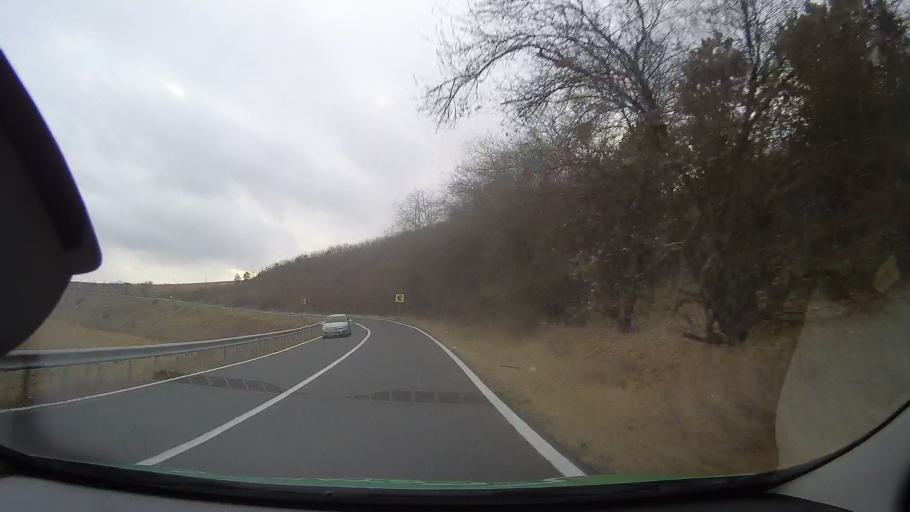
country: RO
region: Constanta
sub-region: Comuna Deleni
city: Deleni
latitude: 44.0991
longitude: 28.0193
